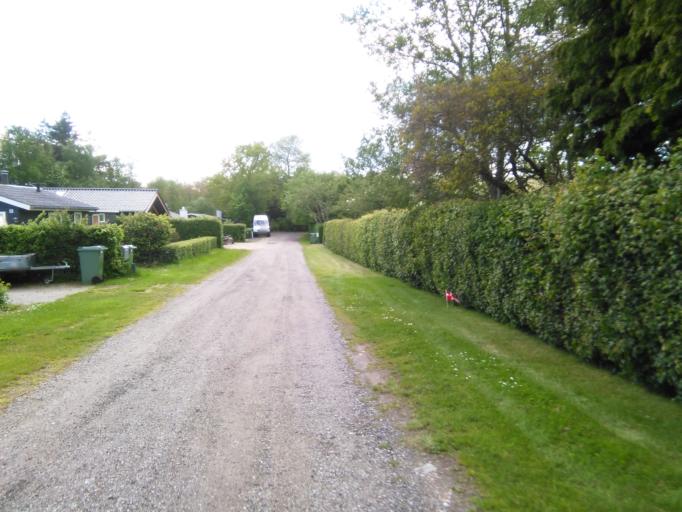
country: DK
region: Central Jutland
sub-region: Arhus Kommune
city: Beder
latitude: 56.0354
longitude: 10.2653
